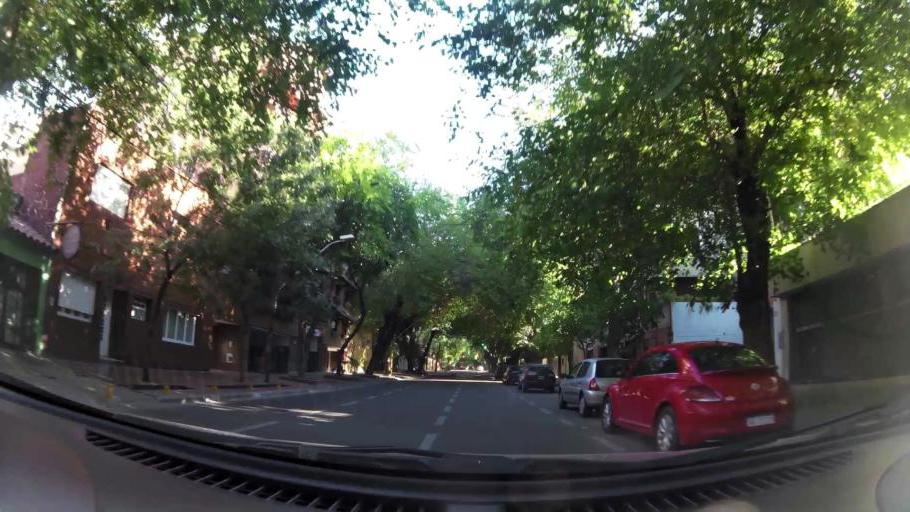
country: AR
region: Mendoza
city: Mendoza
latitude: -32.8907
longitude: -68.8475
